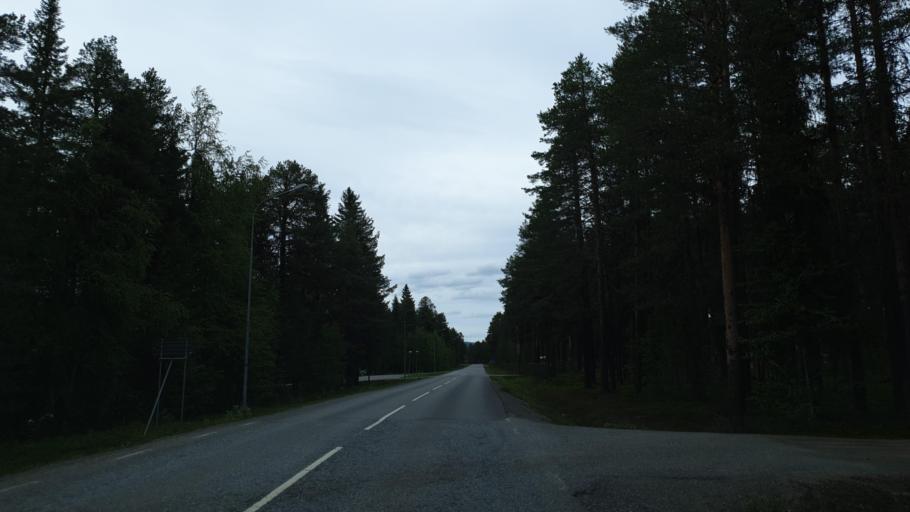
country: SE
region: Vaesterbotten
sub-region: Sorsele Kommun
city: Sorsele
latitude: 65.5454
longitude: 17.5080
